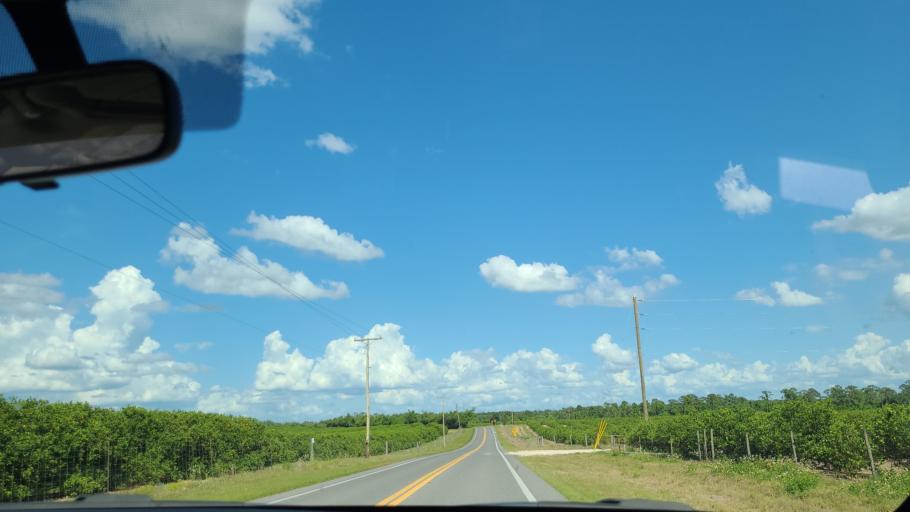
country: US
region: Florida
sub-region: Polk County
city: Babson Park
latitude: 27.9251
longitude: -81.4727
